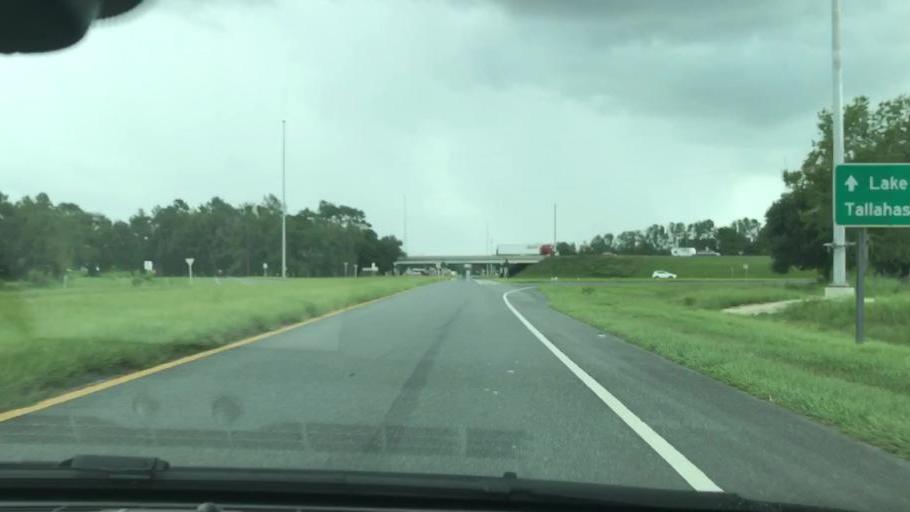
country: US
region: Florida
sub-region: Madison County
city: Madison
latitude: 30.3820
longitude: -83.2989
